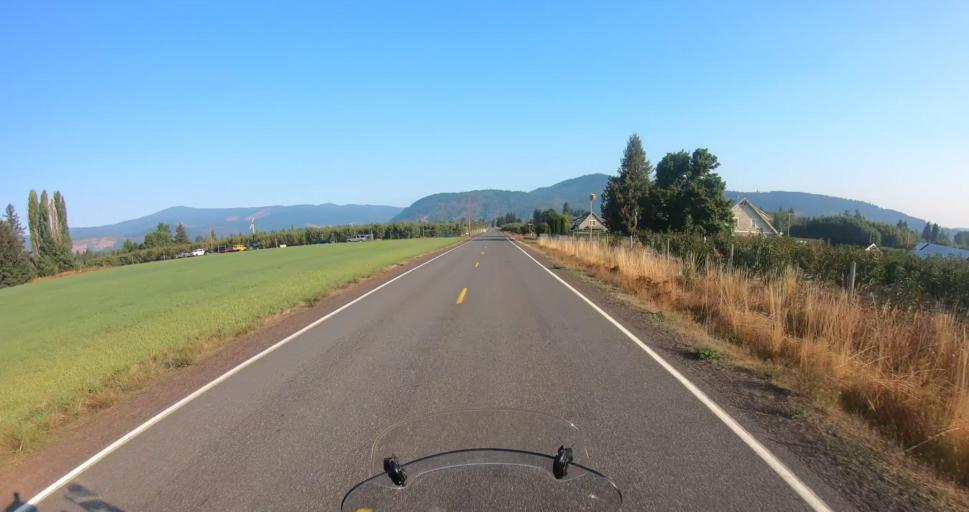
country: US
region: Oregon
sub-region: Hood River County
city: Odell
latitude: 45.5410
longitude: -121.6097
